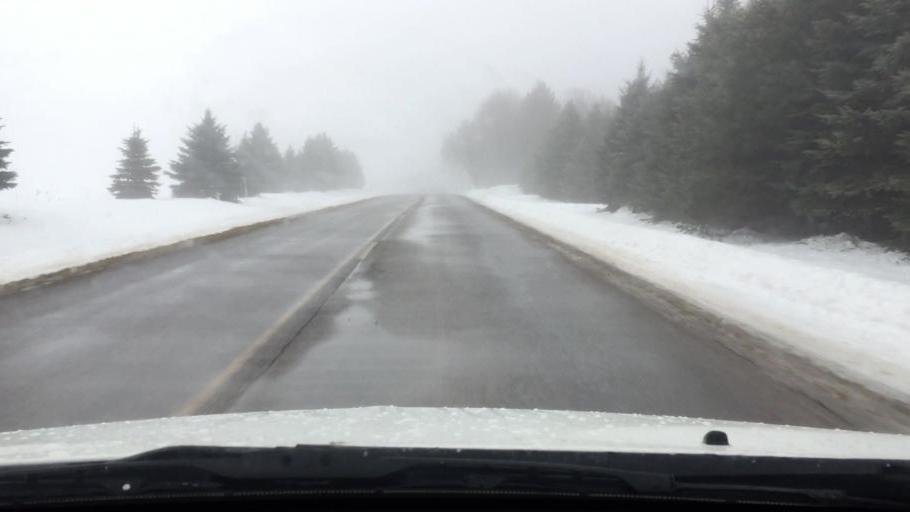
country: US
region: Michigan
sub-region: Charlevoix County
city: East Jordan
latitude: 45.1216
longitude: -85.1801
